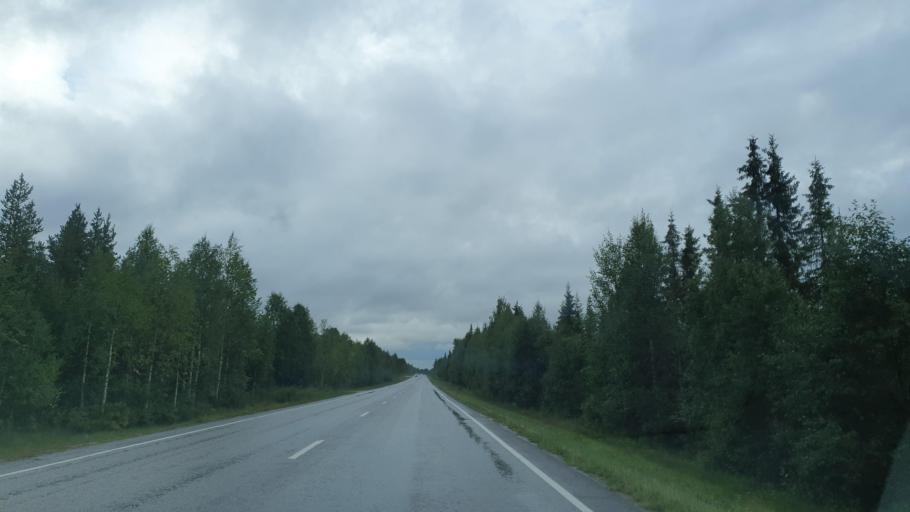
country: FI
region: Lapland
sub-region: Tunturi-Lappi
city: Kolari
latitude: 67.2449
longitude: 23.8769
